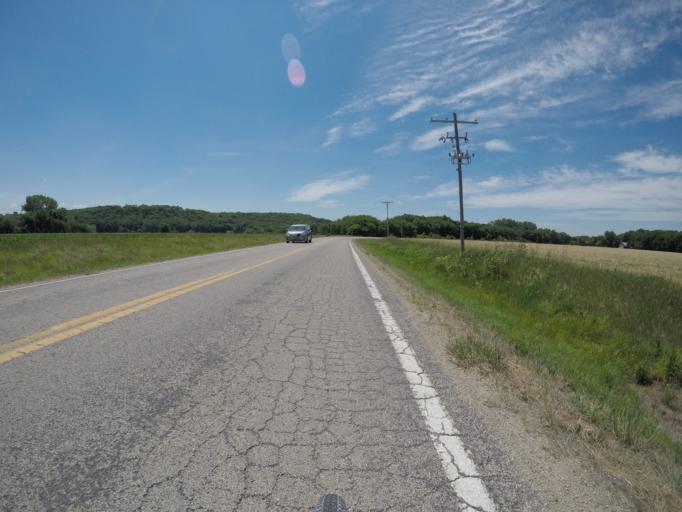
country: US
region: Kansas
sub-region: Wabaunsee County
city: Alma
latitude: 39.0491
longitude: -96.2470
